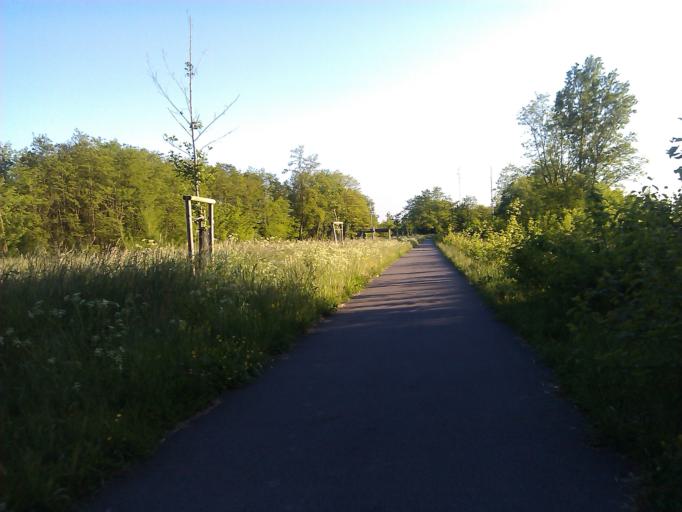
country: FR
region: Auvergne
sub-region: Departement de l'Allier
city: Dompierre-sur-Besbre
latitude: 46.5359
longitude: 3.7045
